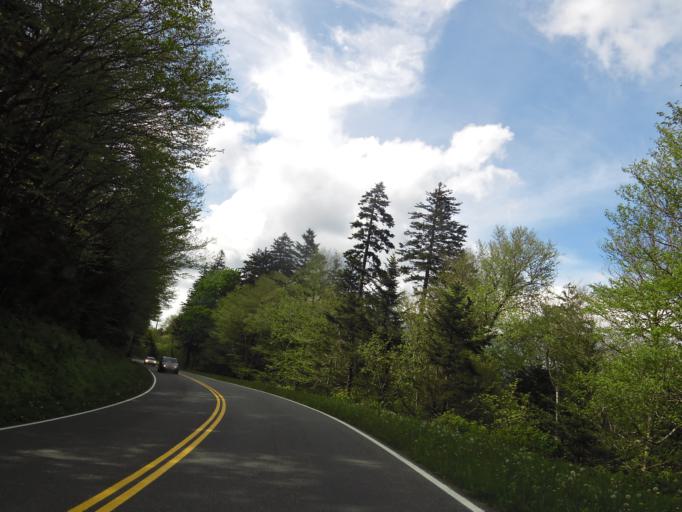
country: US
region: Tennessee
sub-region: Sevier County
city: Gatlinburg
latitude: 35.5926
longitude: -83.4612
